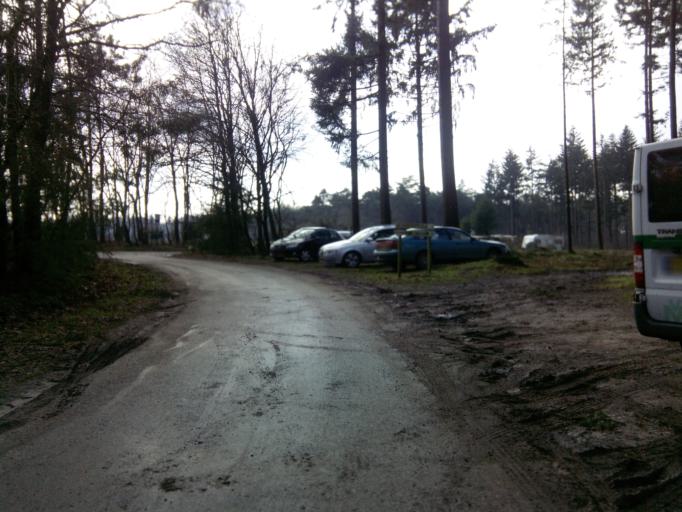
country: NL
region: Utrecht
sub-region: Gemeente Utrechtse Heuvelrug
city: Leersum
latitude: 52.0431
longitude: 5.4486
